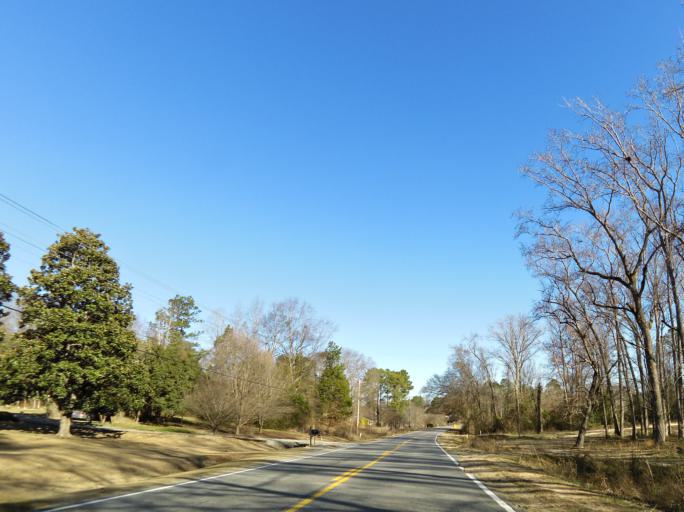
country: US
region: Georgia
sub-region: Bibb County
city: West Point
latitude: 32.7649
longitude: -83.7592
